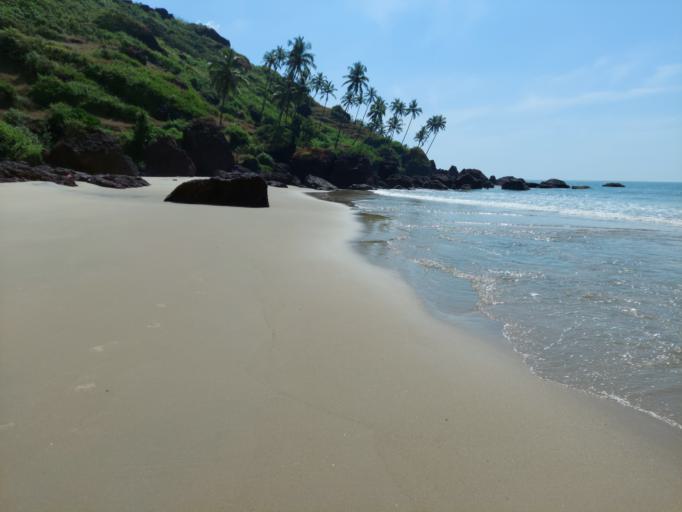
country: IN
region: Maharashtra
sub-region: Sindhudurg
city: Vengurla
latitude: 15.9183
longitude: 73.5674
